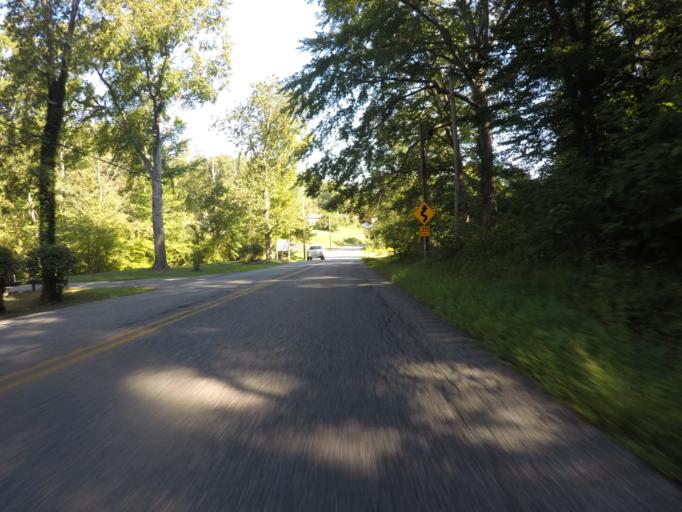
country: US
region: Kentucky
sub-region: Greenup County
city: Russell
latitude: 38.4992
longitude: -82.6964
